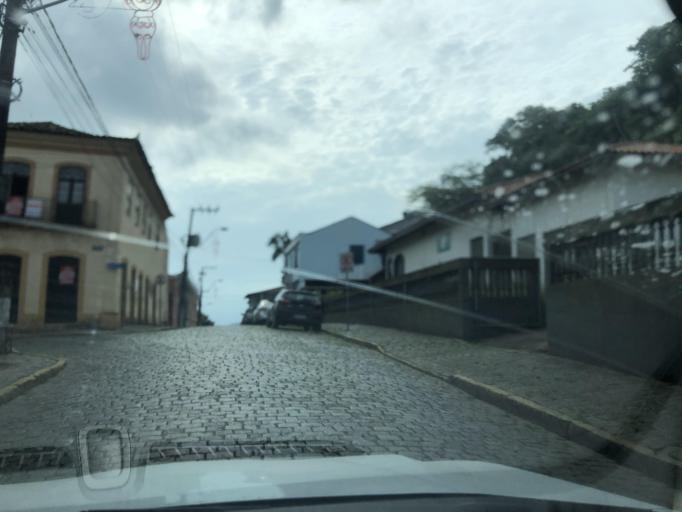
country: BR
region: Santa Catarina
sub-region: Sao Francisco Do Sul
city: Sao Francisco do Sul
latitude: -26.2422
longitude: -48.6382
